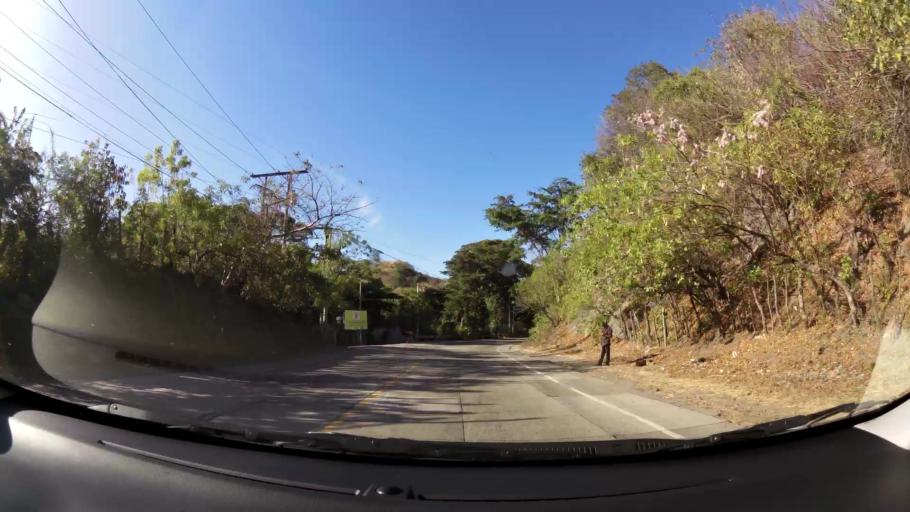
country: SV
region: Santa Ana
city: Texistepeque
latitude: 14.1399
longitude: -89.5135
